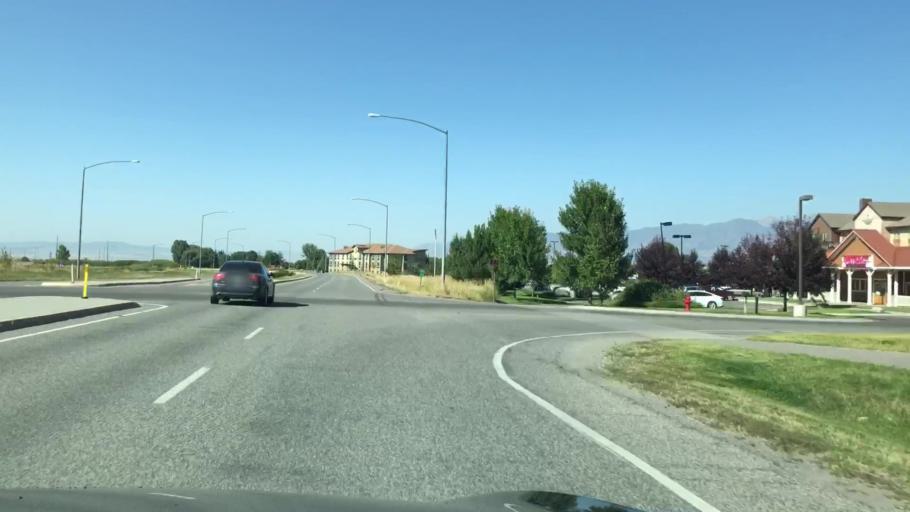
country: US
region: Montana
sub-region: Gallatin County
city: Bozeman
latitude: 45.7146
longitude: -111.0684
